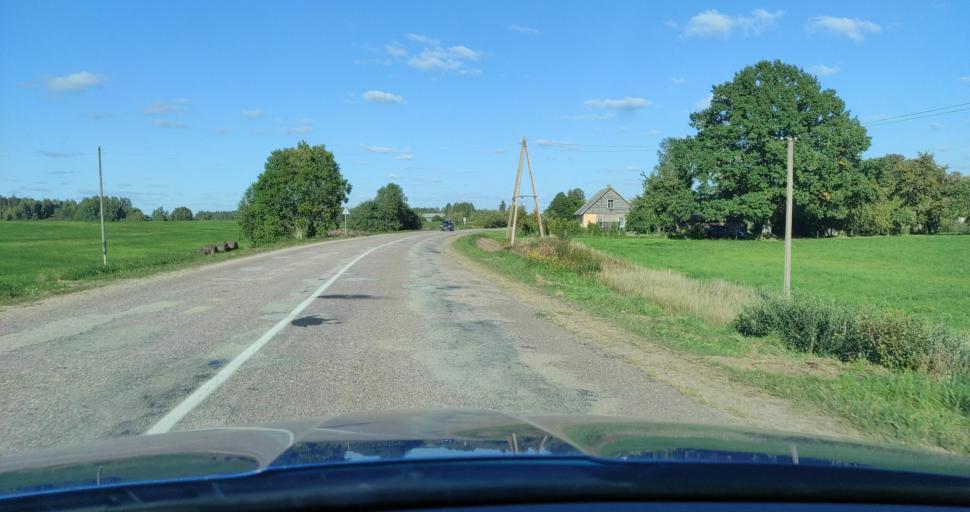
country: LV
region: Skrunda
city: Skrunda
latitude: 56.8092
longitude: 22.0143
